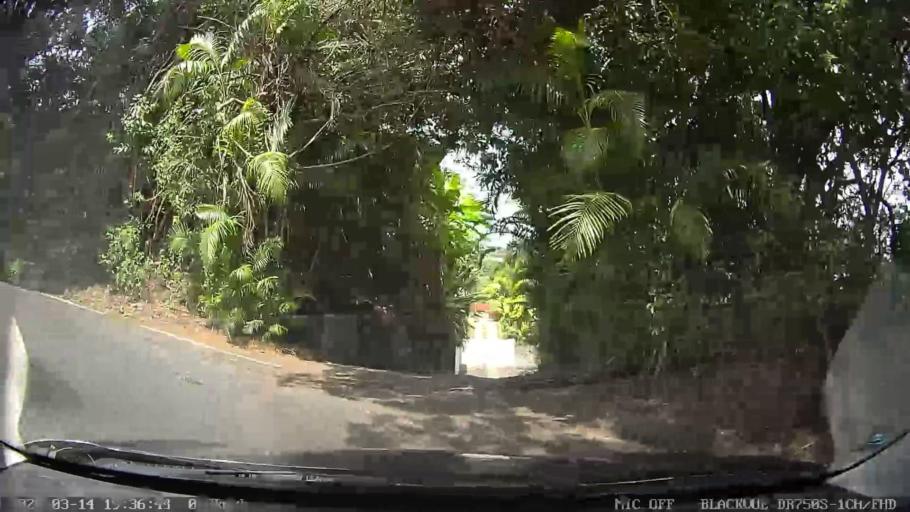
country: RE
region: Reunion
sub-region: Reunion
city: Sainte-Marie
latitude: -20.9421
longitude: 55.5222
